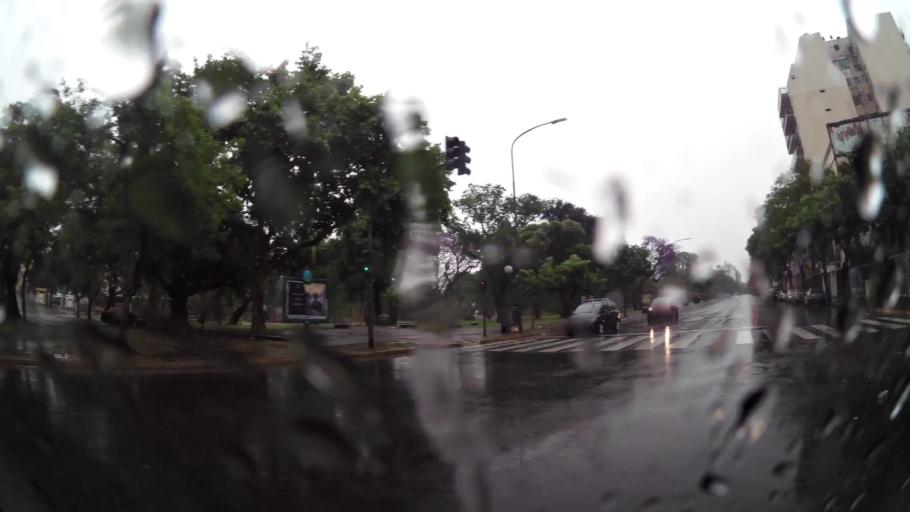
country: AR
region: Buenos Aires F.D.
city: Buenos Aires
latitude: -34.6325
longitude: -58.3839
